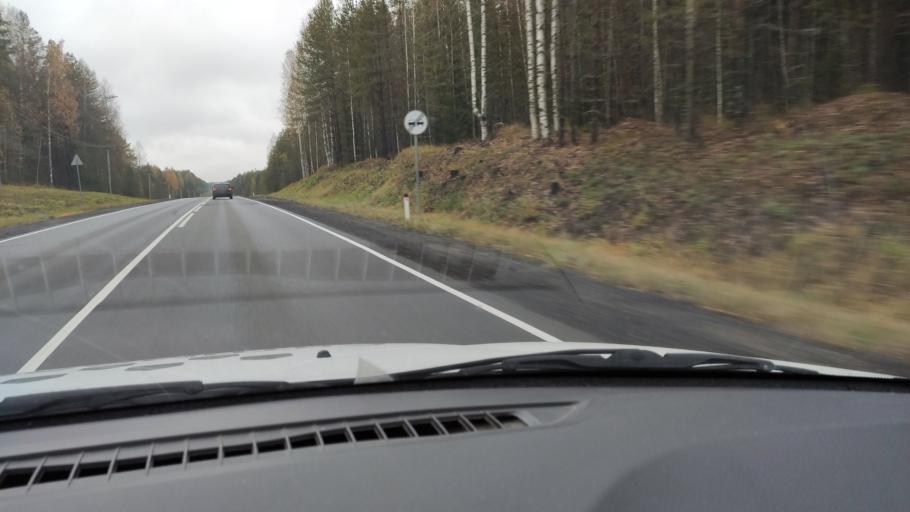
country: RU
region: Kirov
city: Belaya Kholunitsa
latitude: 58.9061
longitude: 51.0235
